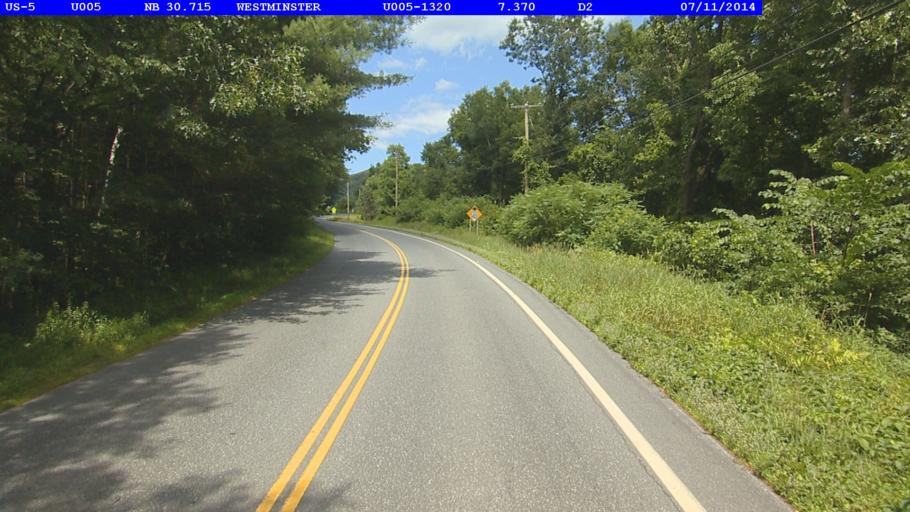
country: US
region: Vermont
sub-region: Windham County
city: Bellows Falls
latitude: 43.1144
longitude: -72.4376
